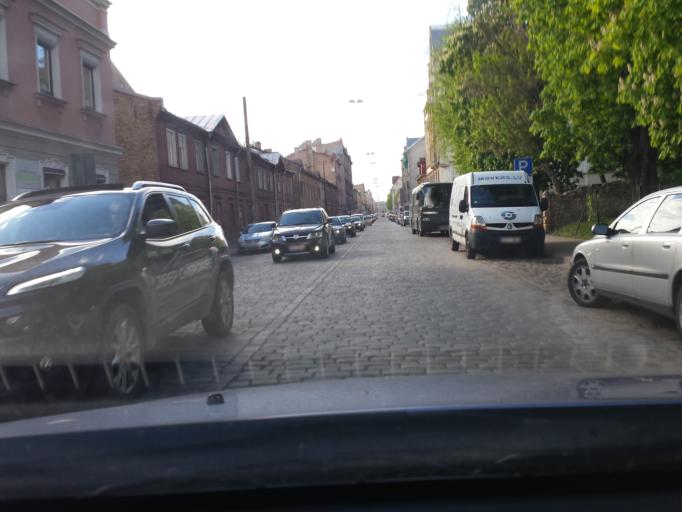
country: LV
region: Riga
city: Riga
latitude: 56.9514
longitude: 24.1455
